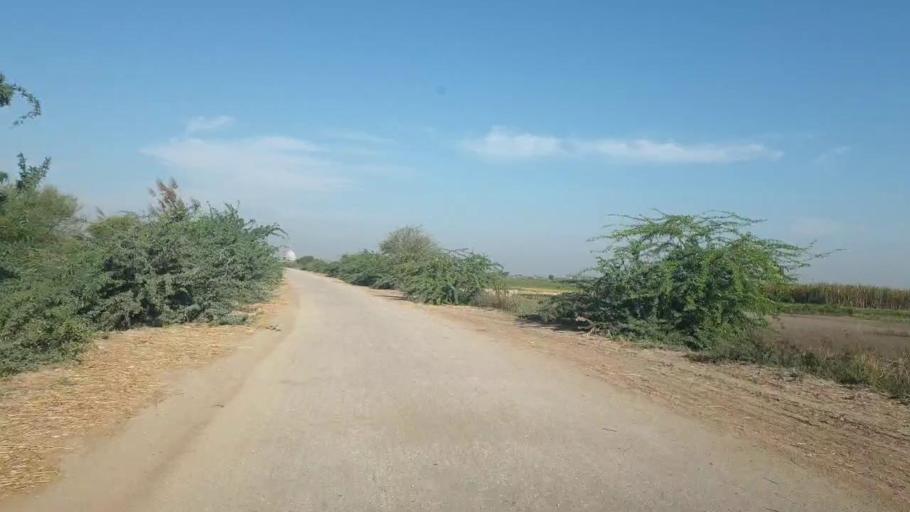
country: PK
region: Sindh
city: Talhar
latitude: 24.9111
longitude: 68.8076
